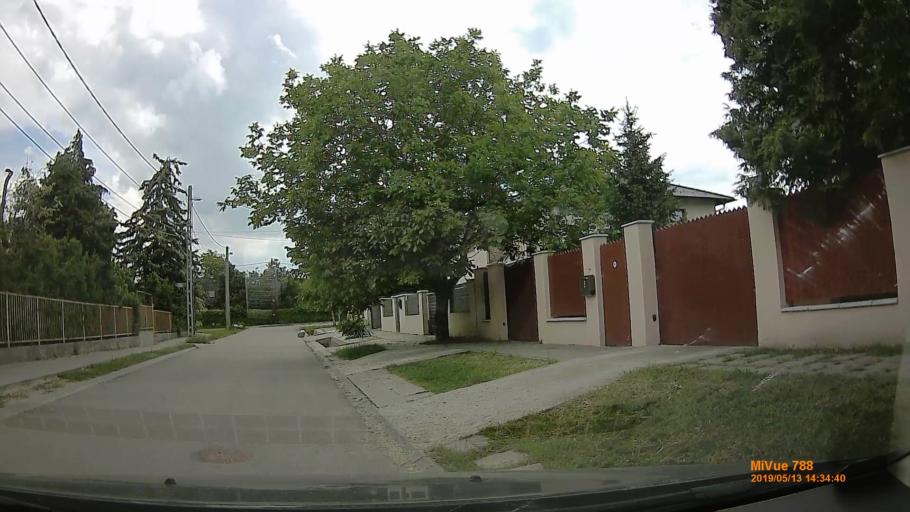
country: HU
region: Budapest
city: Budapest XXII. keruelet
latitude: 47.4235
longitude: 19.0091
